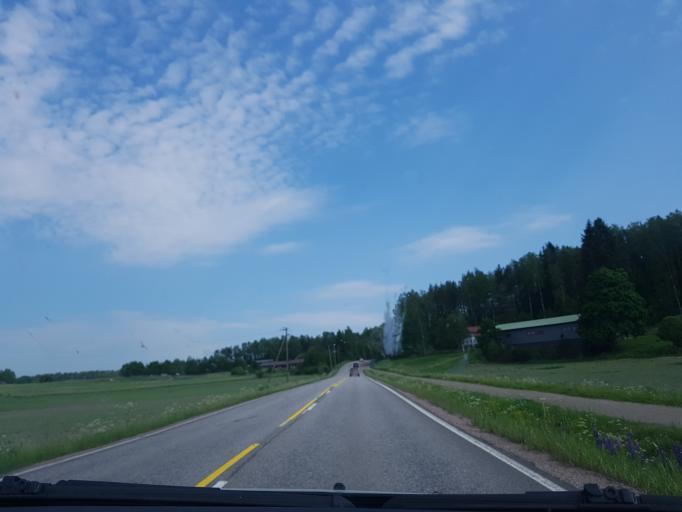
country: FI
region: Uusimaa
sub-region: Helsinki
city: Vihti
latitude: 60.3205
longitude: 24.4037
